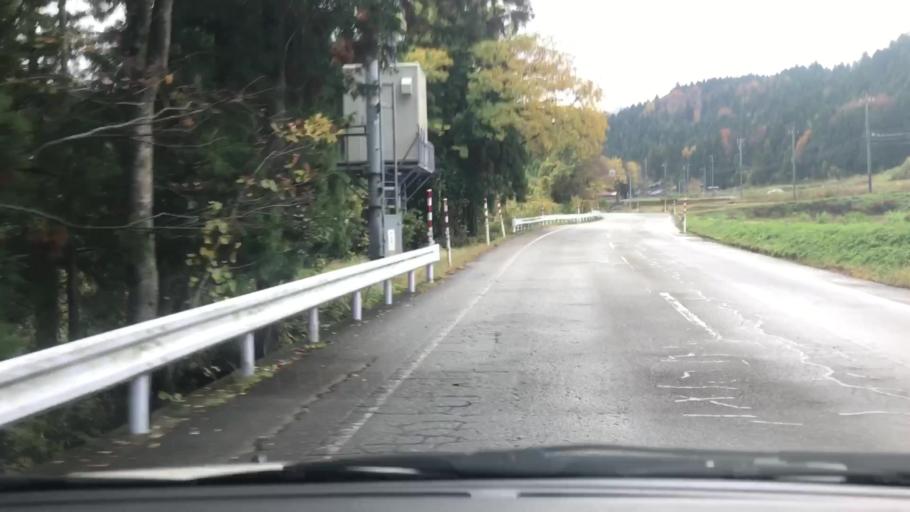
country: JP
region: Toyama
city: Kamiichi
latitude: 36.5869
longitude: 137.3218
